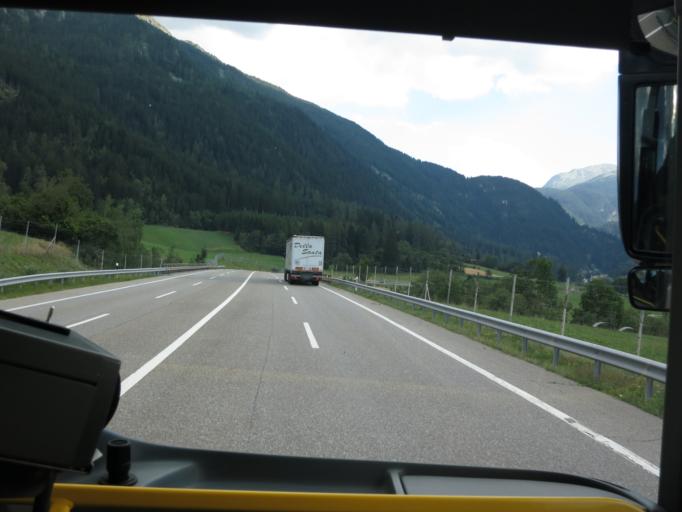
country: CH
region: Grisons
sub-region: Hinterrhein District
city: Thusis
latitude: 46.6130
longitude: 9.4329
